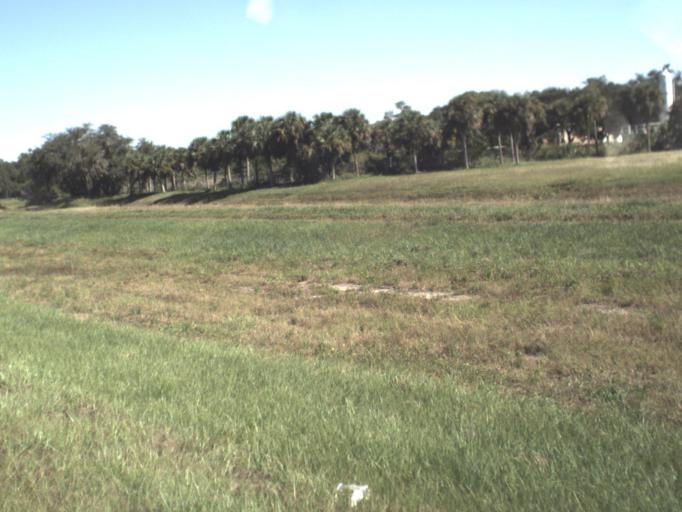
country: US
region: Florida
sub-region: Hendry County
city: Port LaBelle
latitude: 26.7682
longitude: -81.3773
